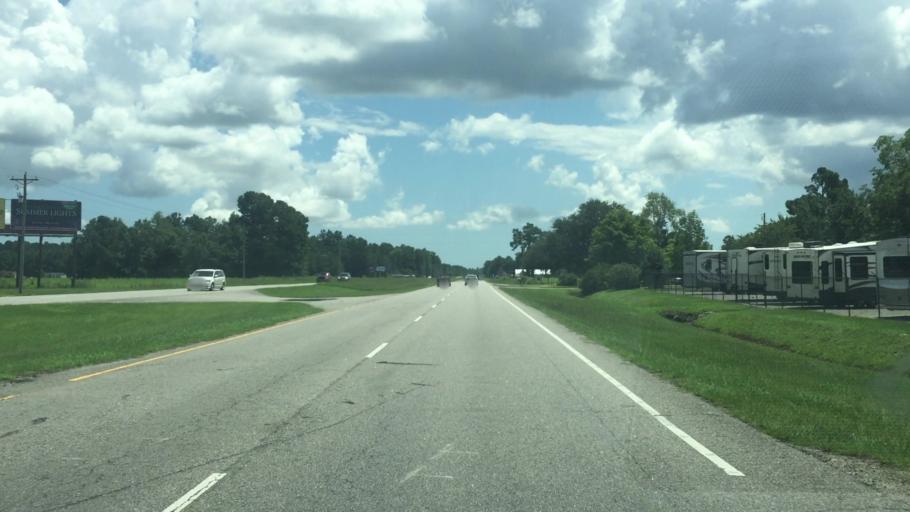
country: US
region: South Carolina
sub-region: Horry County
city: Loris
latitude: 33.9884
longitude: -78.7478
